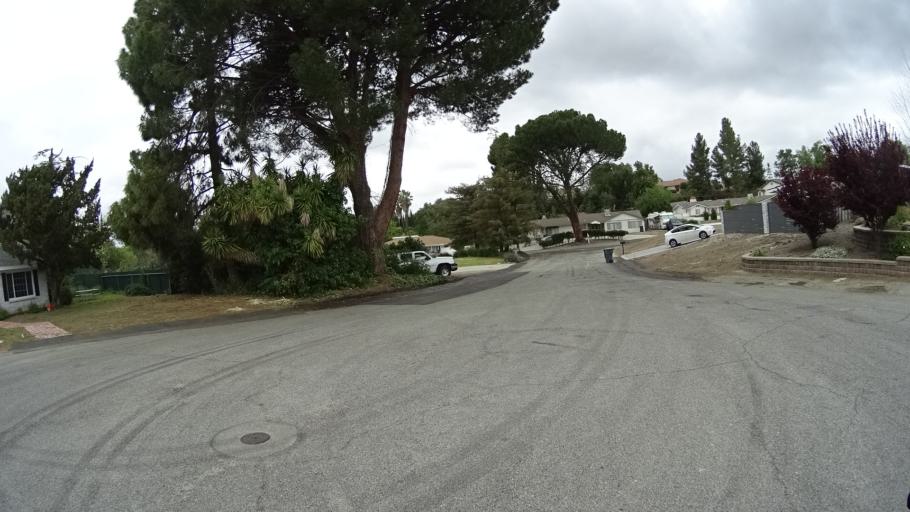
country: US
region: California
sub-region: Ventura County
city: Thousand Oaks
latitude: 34.2151
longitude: -118.8757
